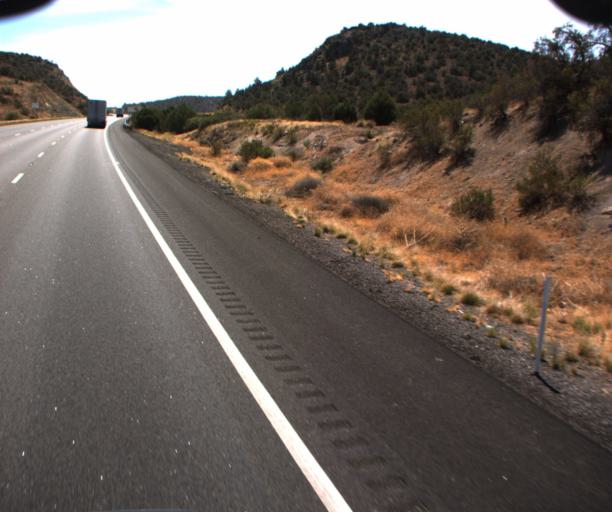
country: US
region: Arizona
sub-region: Mohave County
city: Peach Springs
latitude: 35.1890
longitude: -113.4231
